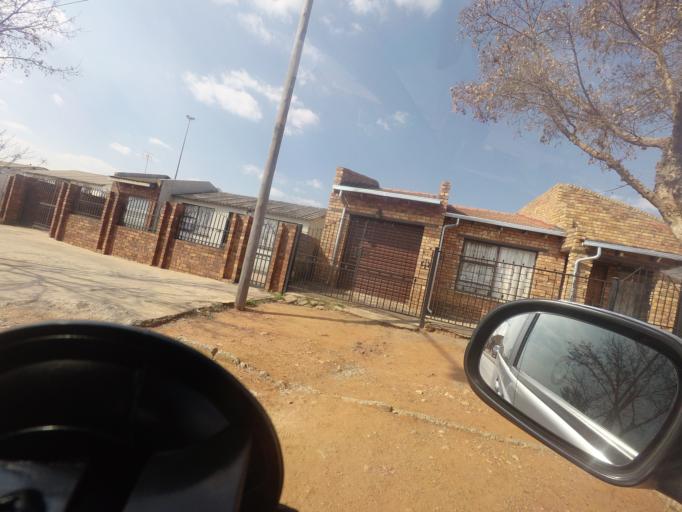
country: ZA
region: Gauteng
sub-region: Sedibeng District Municipality
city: Heidelberg
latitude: -26.5512
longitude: 28.3298
